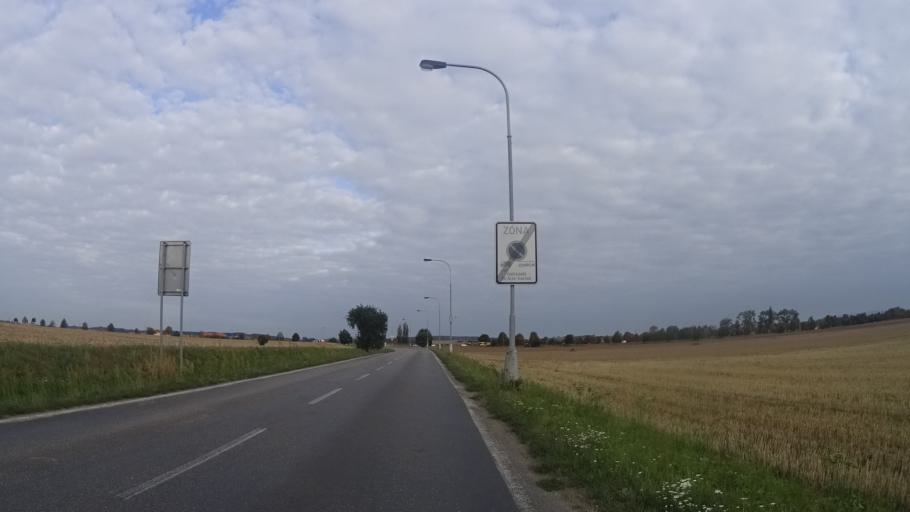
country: CZ
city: Stezery
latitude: 50.2083
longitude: 15.7866
